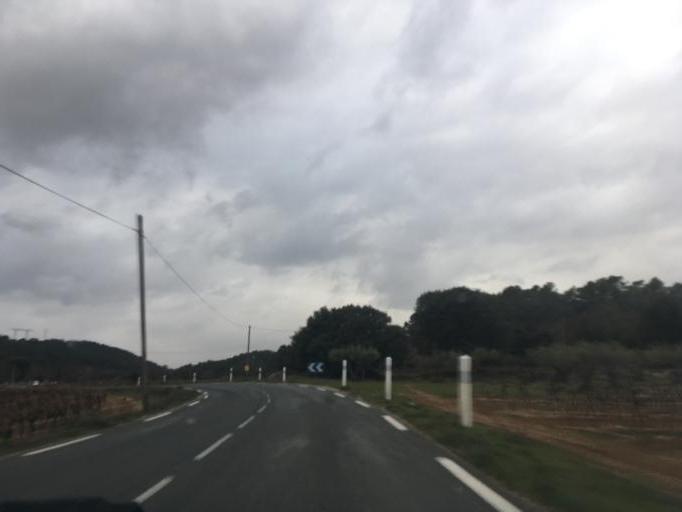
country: FR
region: Provence-Alpes-Cote d'Azur
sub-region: Departement du Var
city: Sainte-Anastasie-sur-Issole
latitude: 43.3403
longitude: 6.1496
